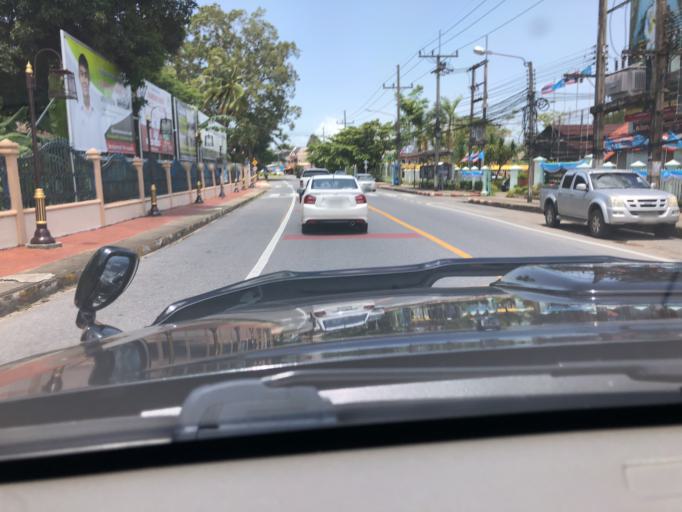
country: TH
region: Krabi
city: Krabi
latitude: 8.0569
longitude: 98.9145
